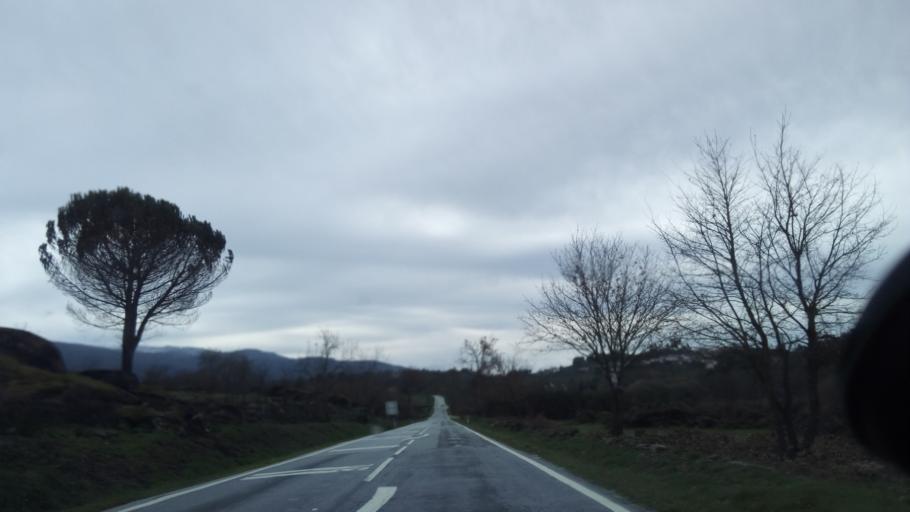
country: PT
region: Guarda
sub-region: Seia
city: Seia
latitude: 40.4984
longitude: -7.6547
